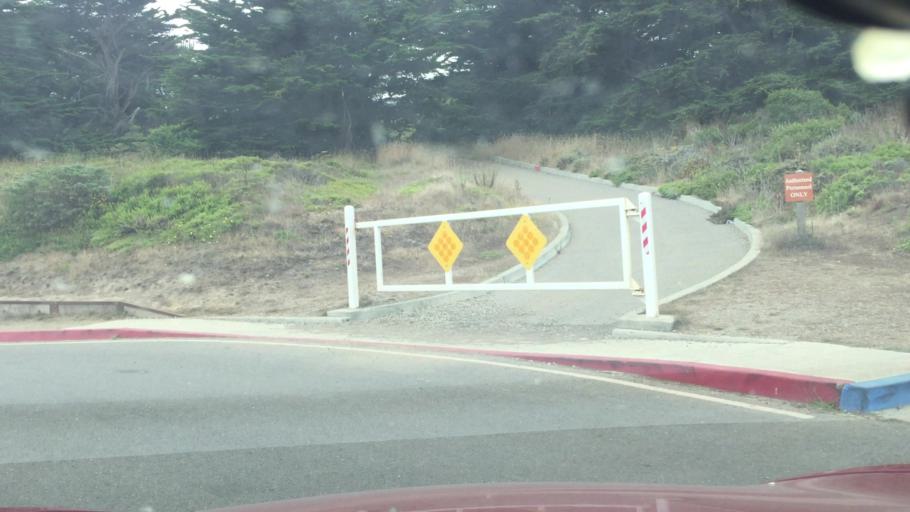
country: US
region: California
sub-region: Marin County
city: Marin City
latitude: 37.8217
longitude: -122.5300
